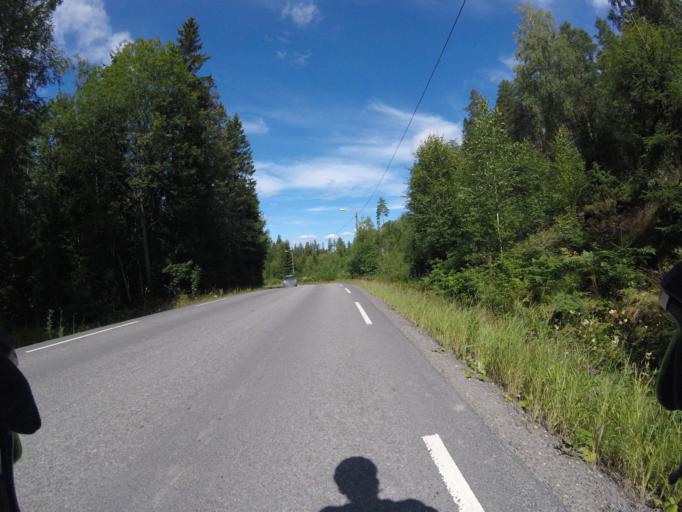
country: NO
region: Akershus
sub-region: Lorenskog
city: Kjenn
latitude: 59.9020
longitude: 10.9679
